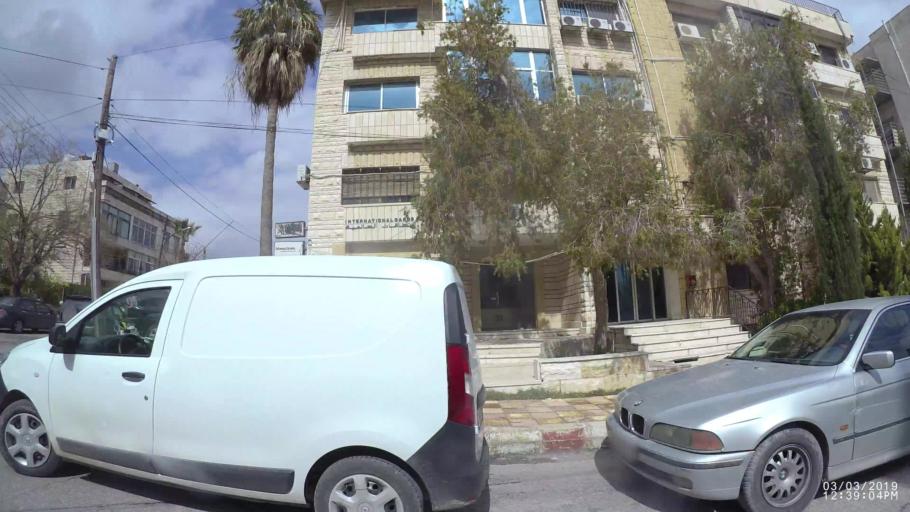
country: JO
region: Amman
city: Amman
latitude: 31.9706
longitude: 35.8994
